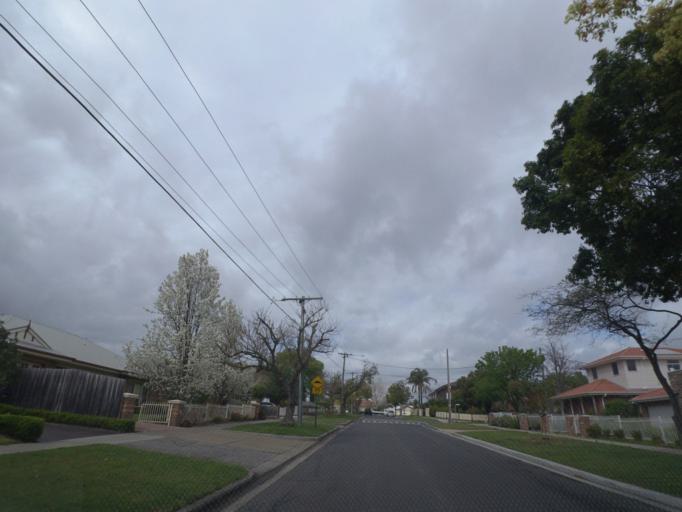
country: AU
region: Victoria
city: Mitcham
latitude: -37.8132
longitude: 145.1894
